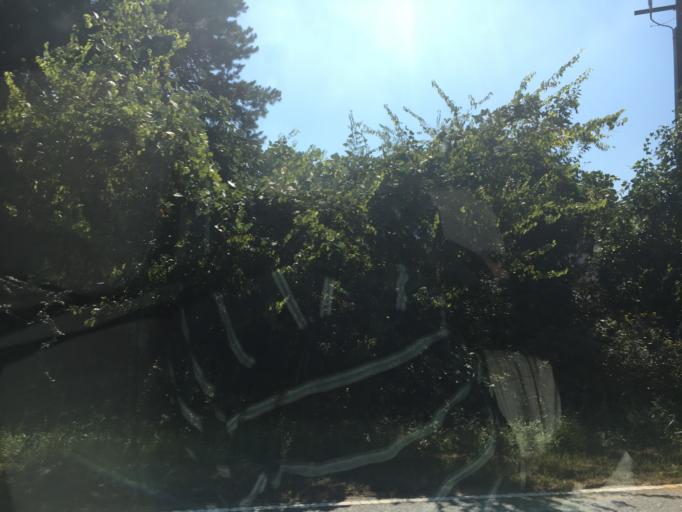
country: US
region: South Carolina
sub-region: Spartanburg County
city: Wellford
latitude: 34.9007
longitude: -82.0806
